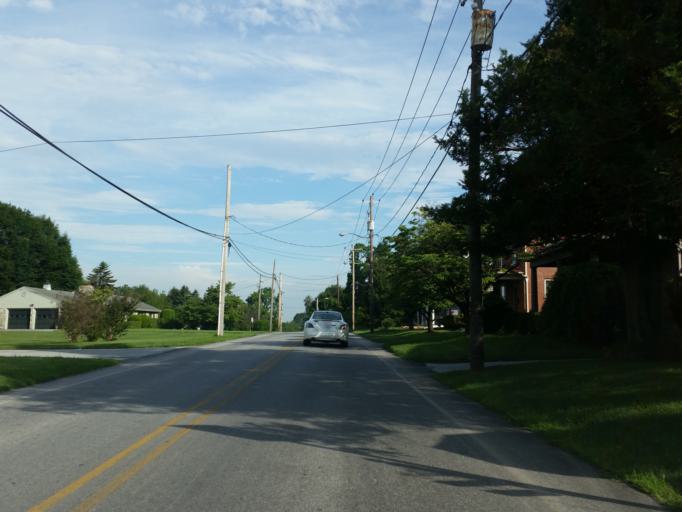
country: US
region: Pennsylvania
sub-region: Lancaster County
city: Strasburg
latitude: 39.9836
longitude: -76.1861
